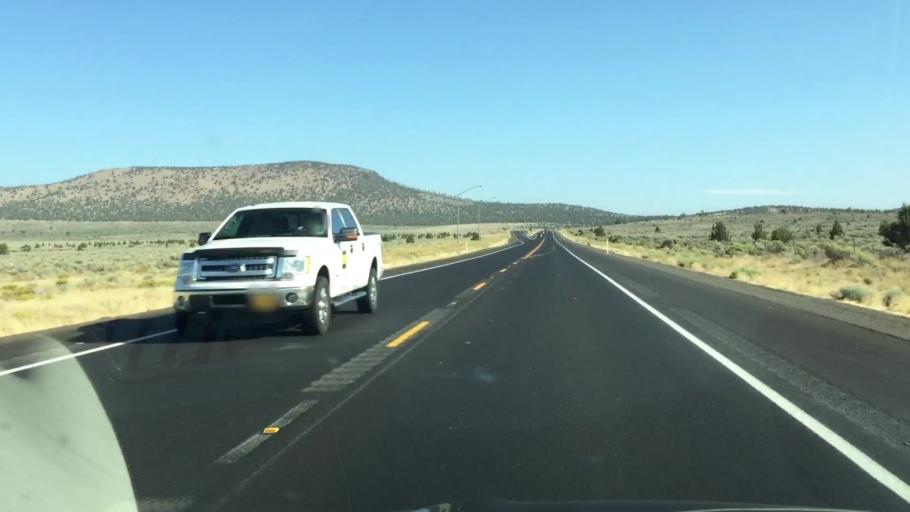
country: US
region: Oregon
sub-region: Jefferson County
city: Culver
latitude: 44.4506
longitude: -121.1995
